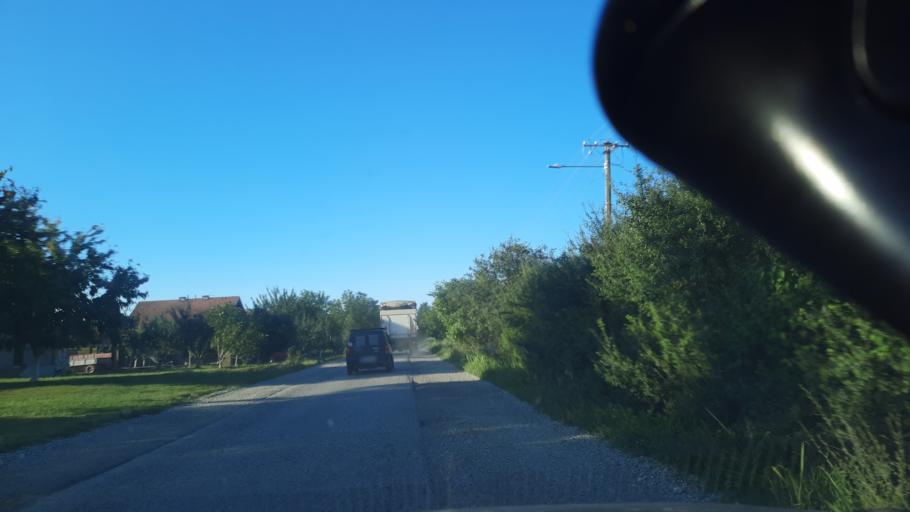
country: RS
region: Autonomna Pokrajina Vojvodina
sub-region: Sremski Okrug
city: Irig
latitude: 45.1124
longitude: 19.9335
